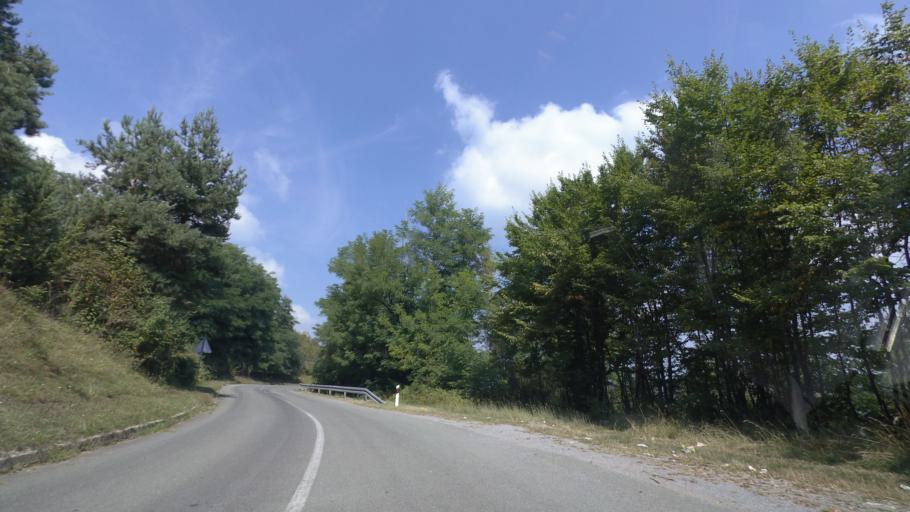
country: BA
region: Federation of Bosnia and Herzegovina
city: Zboriste
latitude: 45.1568
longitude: 16.1413
